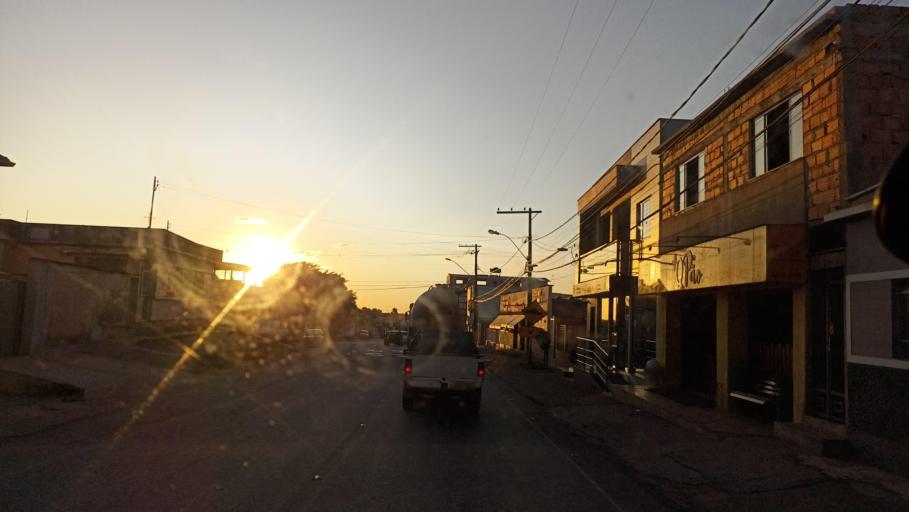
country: BR
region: Minas Gerais
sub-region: Sao Joao Del Rei
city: Sao Joao del Rei
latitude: -21.2440
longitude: -44.4148
